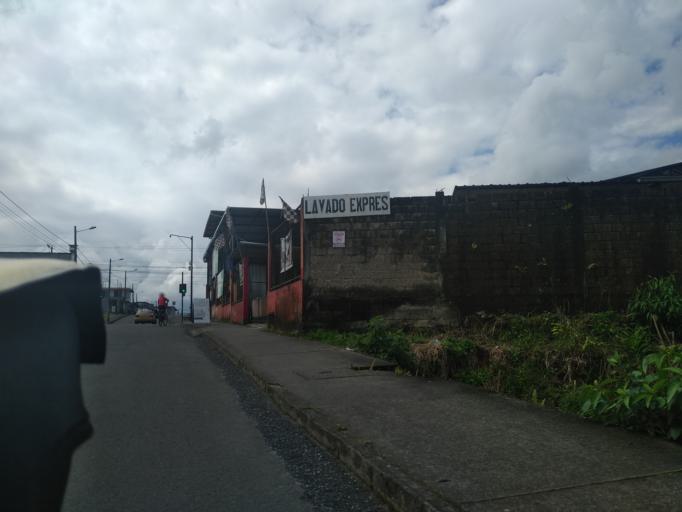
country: EC
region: Pastaza
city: Puyo
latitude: -1.4890
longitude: -78.0031
